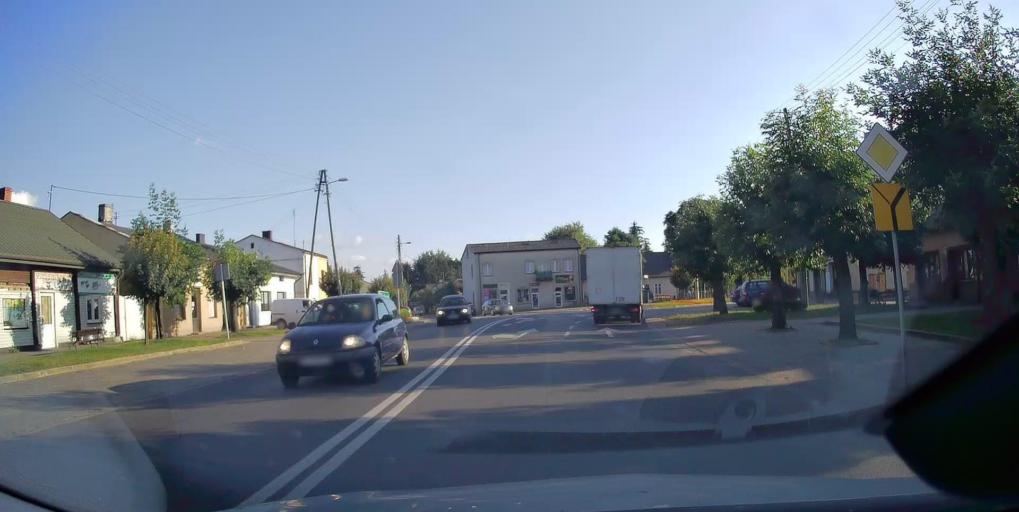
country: PL
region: Lodz Voivodeship
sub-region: Powiat rawski
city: Biala Rawska
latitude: 51.8068
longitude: 20.4710
